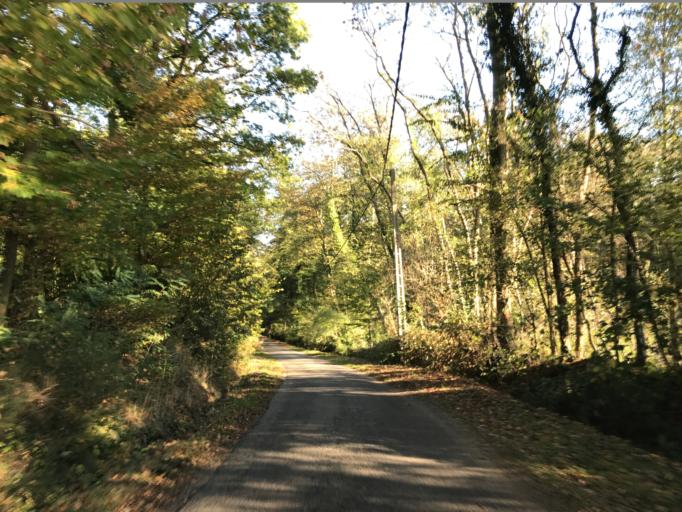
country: FR
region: Haute-Normandie
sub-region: Departement de l'Eure
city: Saint-Aubin-sur-Gaillon
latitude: 49.0744
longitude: 1.2692
